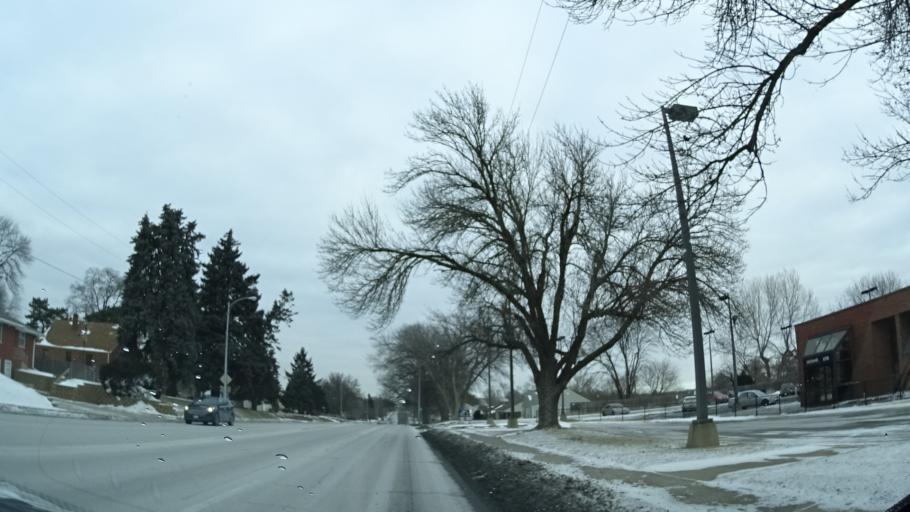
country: US
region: Nebraska
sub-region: Douglas County
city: Omaha
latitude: 41.2286
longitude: -95.9758
